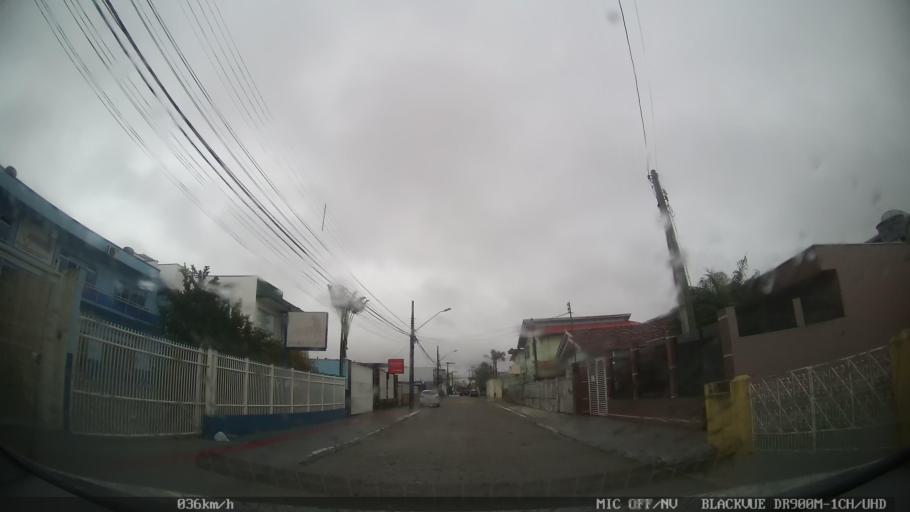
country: BR
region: Santa Catarina
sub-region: Itajai
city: Itajai
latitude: -26.8961
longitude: -48.6741
